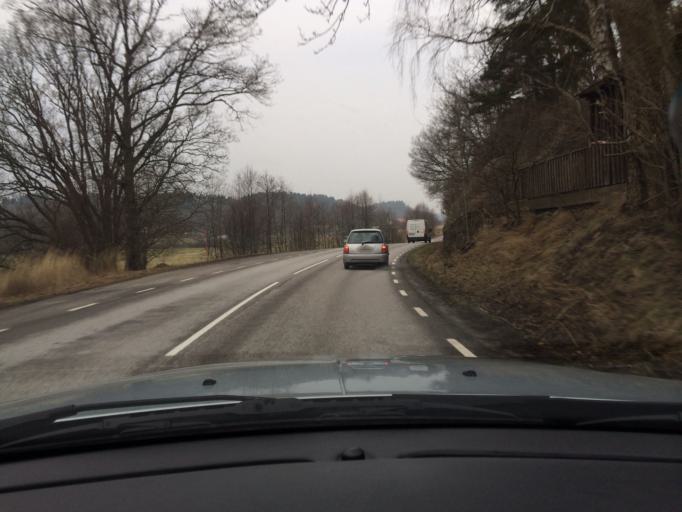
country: SE
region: Vaestra Goetaland
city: Svanesund
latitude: 58.1105
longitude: 11.8515
